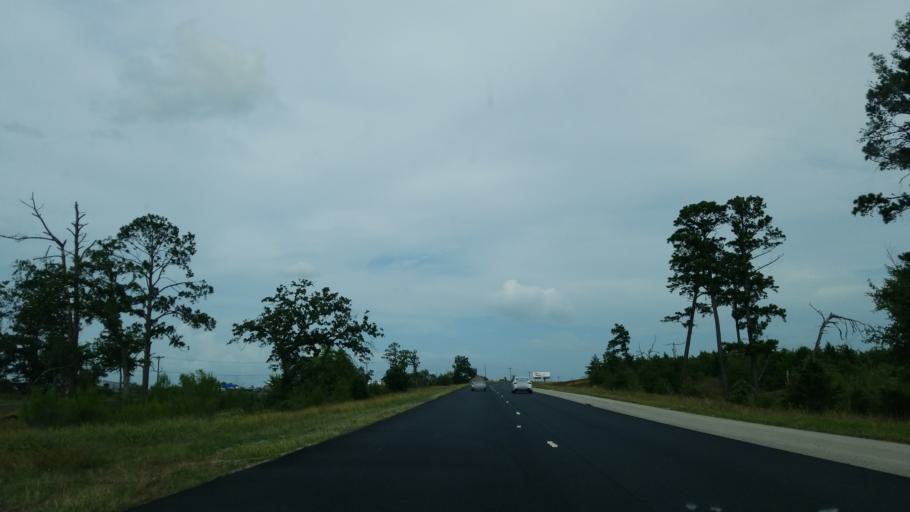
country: US
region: Texas
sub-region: Bastrop County
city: Bastrop
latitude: 30.0904
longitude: -97.2564
